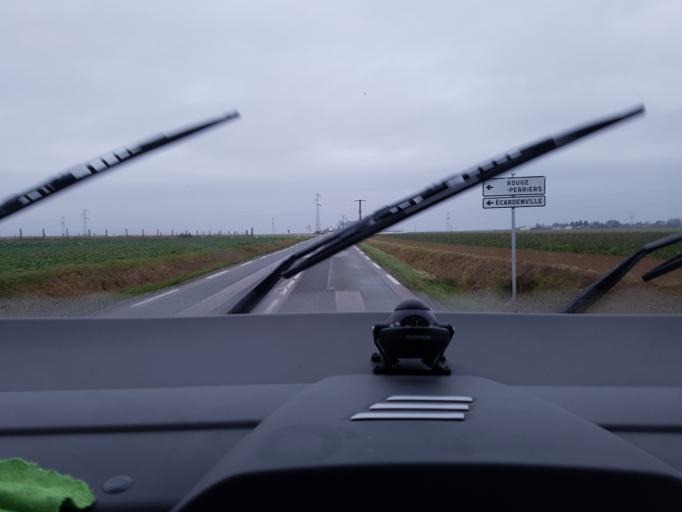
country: FR
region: Haute-Normandie
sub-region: Departement de l'Eure
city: Le Neubourg
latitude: 49.1138
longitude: 0.8482
